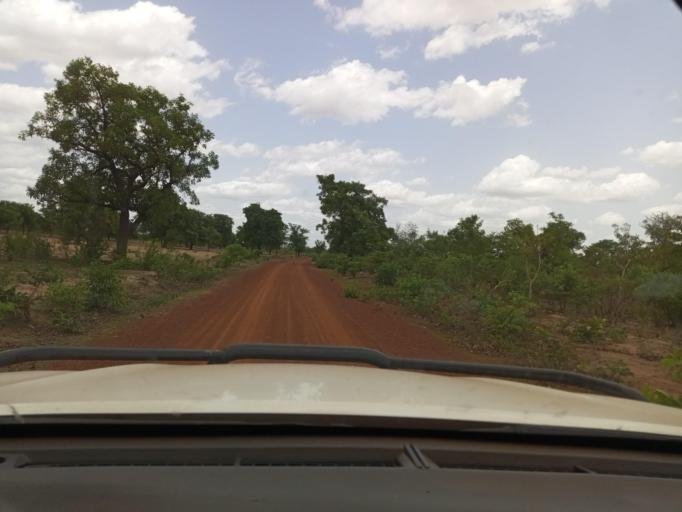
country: ML
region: Sikasso
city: Kolondieba
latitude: 11.7465
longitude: -6.7517
